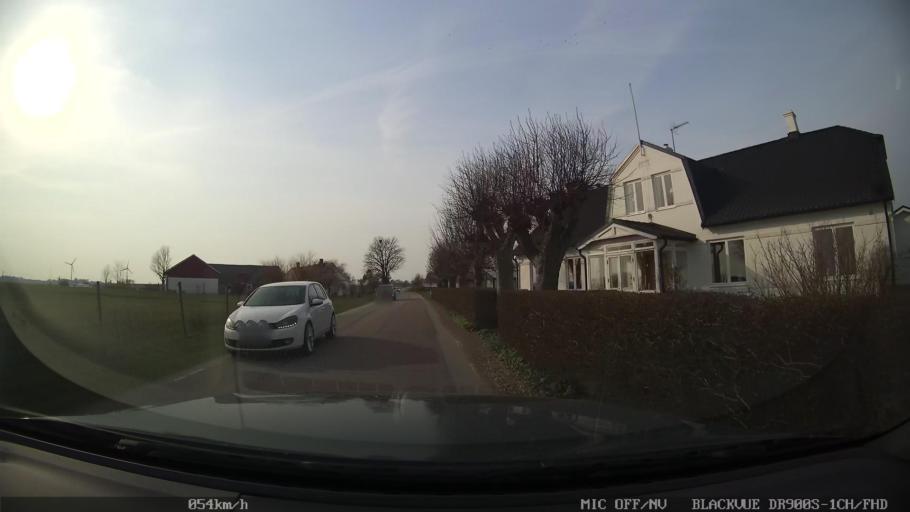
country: SE
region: Skane
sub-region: Ystads Kommun
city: Ystad
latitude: 55.4670
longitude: 13.8120
